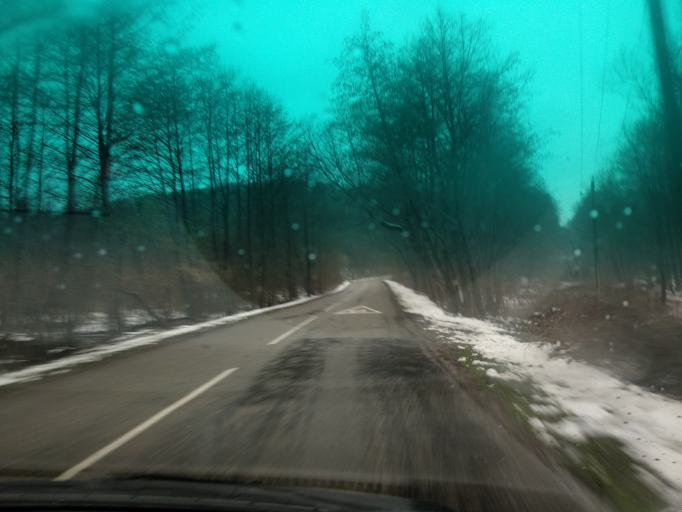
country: RU
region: Krasnodarskiy
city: Khadyzhensk
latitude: 44.2274
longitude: 39.3852
